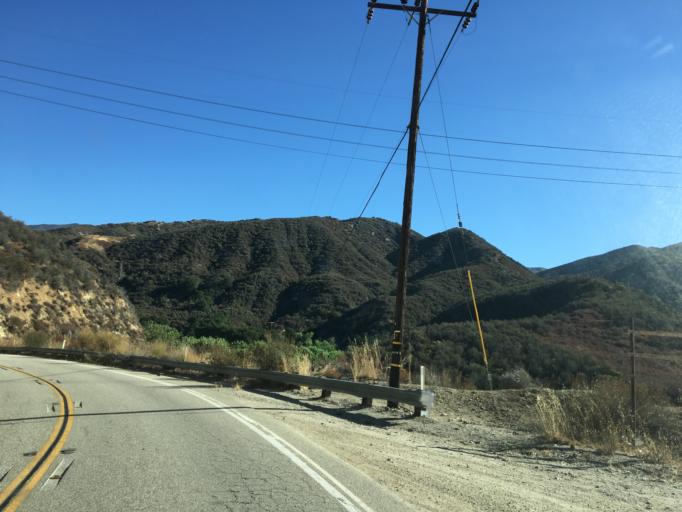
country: US
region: California
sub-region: Los Angeles County
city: Castaic
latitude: 34.6034
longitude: -118.5571
